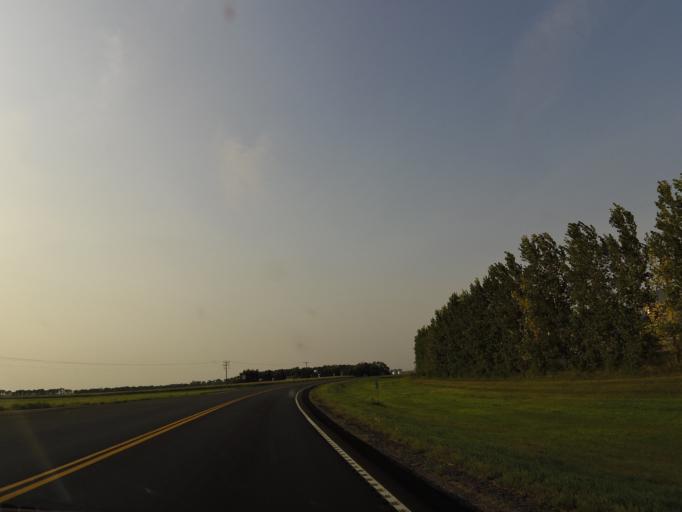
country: US
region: North Dakota
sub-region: Traill County
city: Mayville
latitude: 47.3560
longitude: -97.3249
